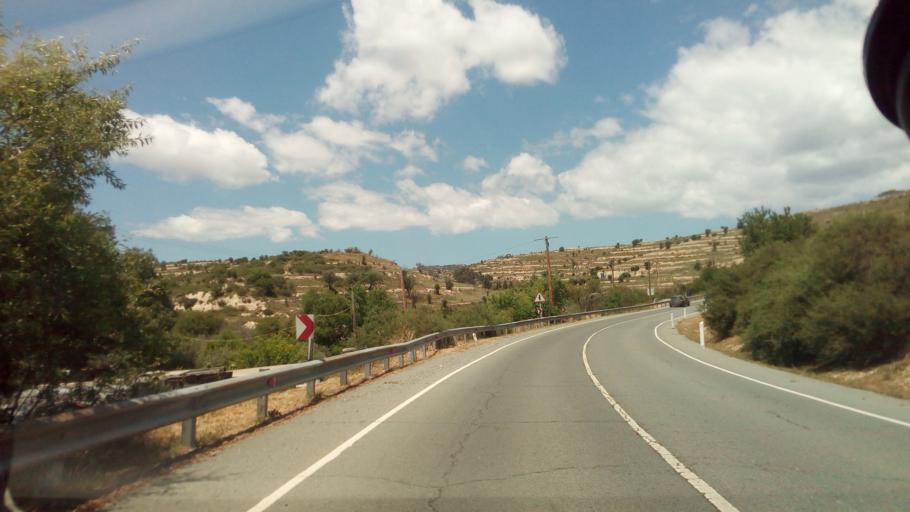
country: CY
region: Limassol
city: Pachna
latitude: 34.7868
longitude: 32.8241
